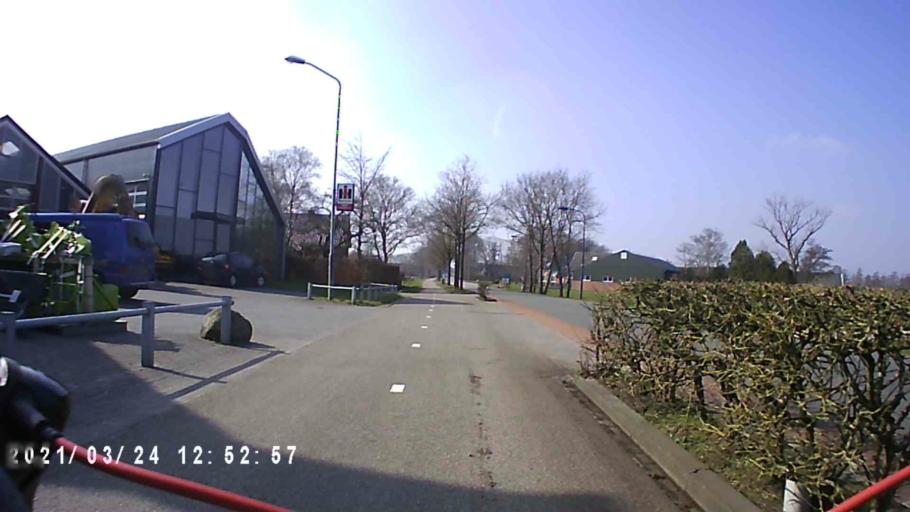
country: NL
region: Groningen
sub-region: Gemeente Leek
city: Leek
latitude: 53.1578
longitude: 6.3209
